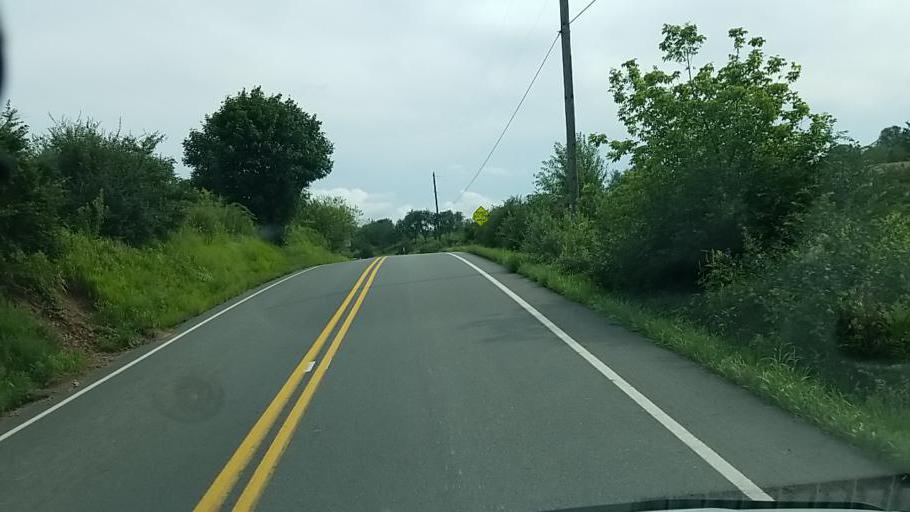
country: US
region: Pennsylvania
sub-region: Dauphin County
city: Elizabethville
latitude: 40.6154
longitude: -76.7837
